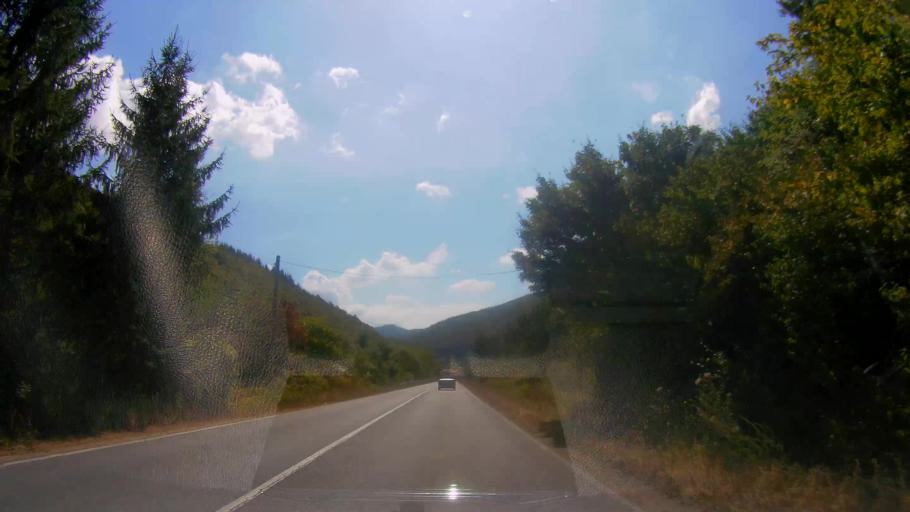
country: BG
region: Stara Zagora
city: Gurkovo
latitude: 42.7446
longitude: 25.7093
